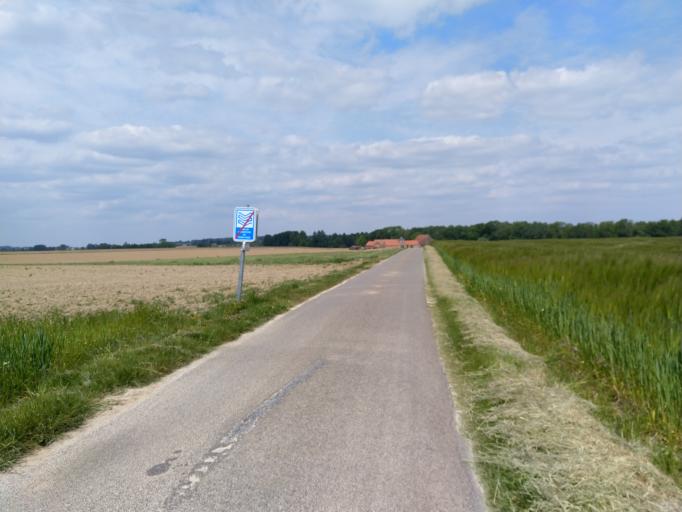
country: BE
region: Wallonia
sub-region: Province du Hainaut
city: Lens
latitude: 50.5662
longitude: 3.9196
